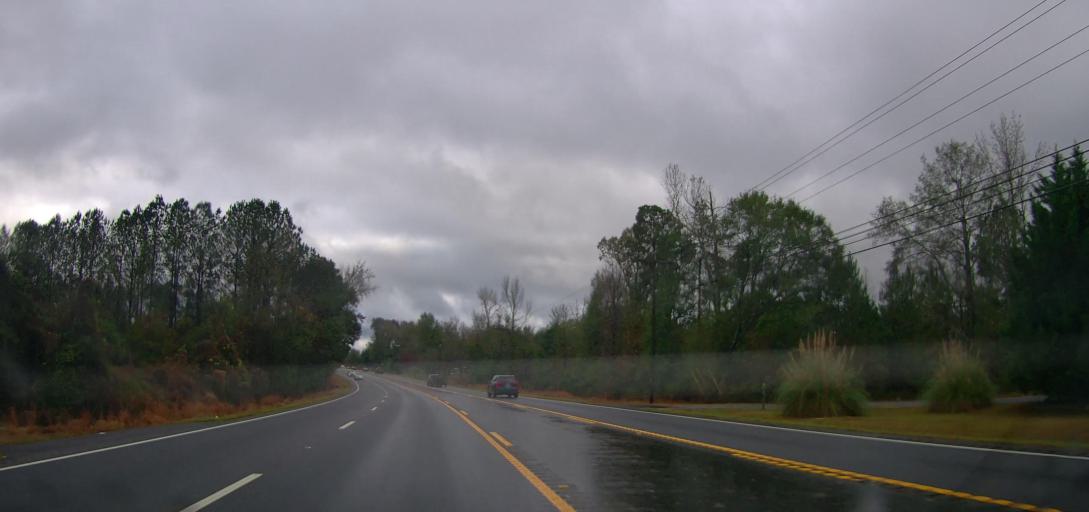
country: US
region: Georgia
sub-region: Clarke County
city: Country Club Estates
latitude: 34.0068
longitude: -83.3870
